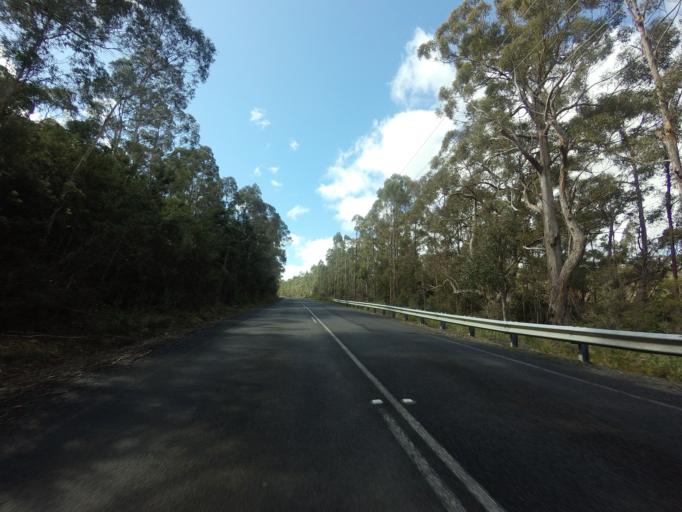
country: AU
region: Tasmania
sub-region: Huon Valley
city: Geeveston
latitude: -43.4154
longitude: 146.9361
